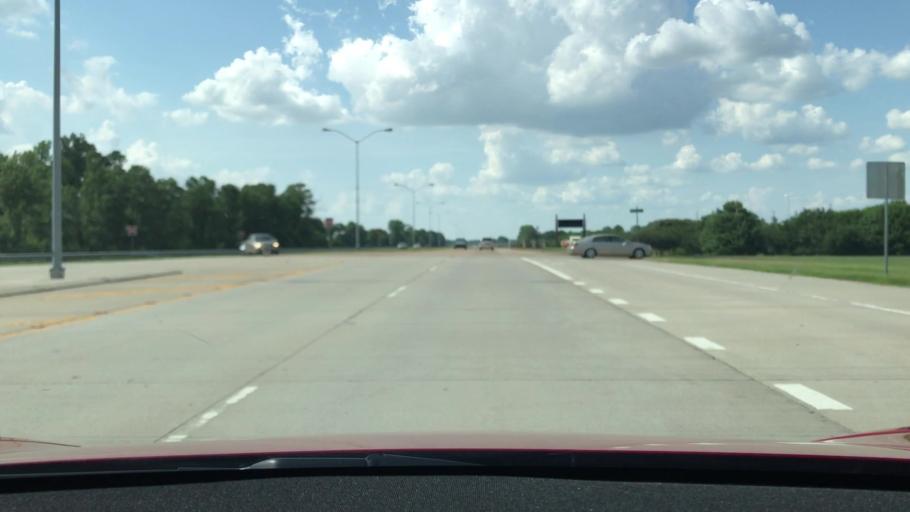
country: US
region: Louisiana
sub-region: Bossier Parish
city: Bossier City
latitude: 32.4618
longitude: -93.6758
